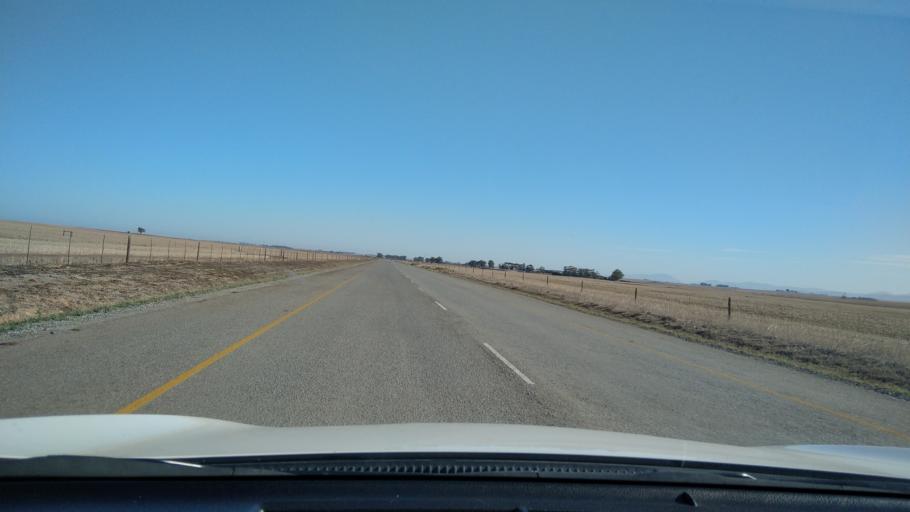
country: ZA
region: Western Cape
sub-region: West Coast District Municipality
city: Moorreesburg
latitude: -33.2982
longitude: 18.6128
